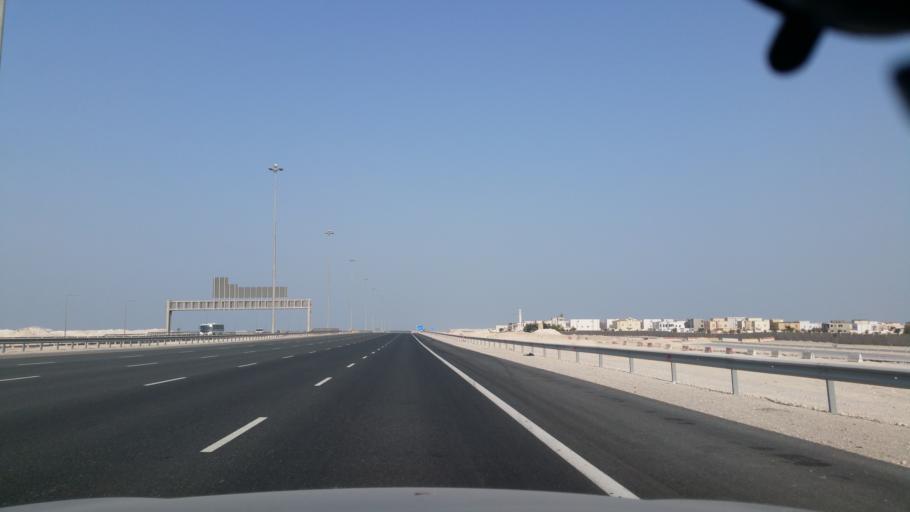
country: QA
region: Baladiyat Umm Salal
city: Umm Salal `Ali
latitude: 25.4530
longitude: 51.4292
